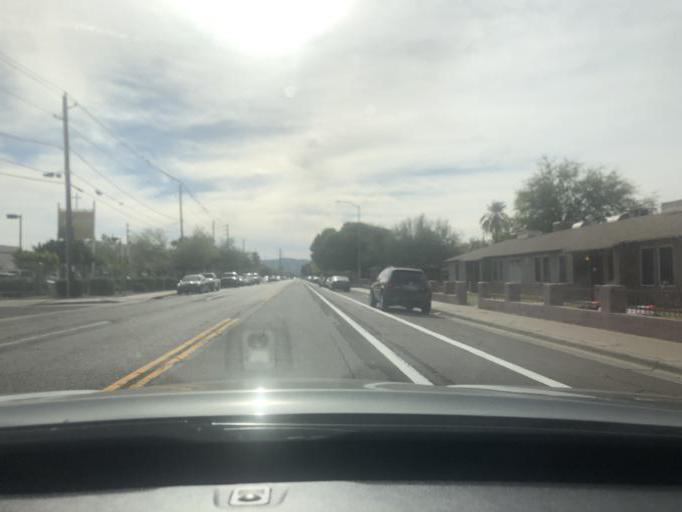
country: US
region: Arizona
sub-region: Maricopa County
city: Phoenix
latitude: 33.4564
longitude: -112.0390
